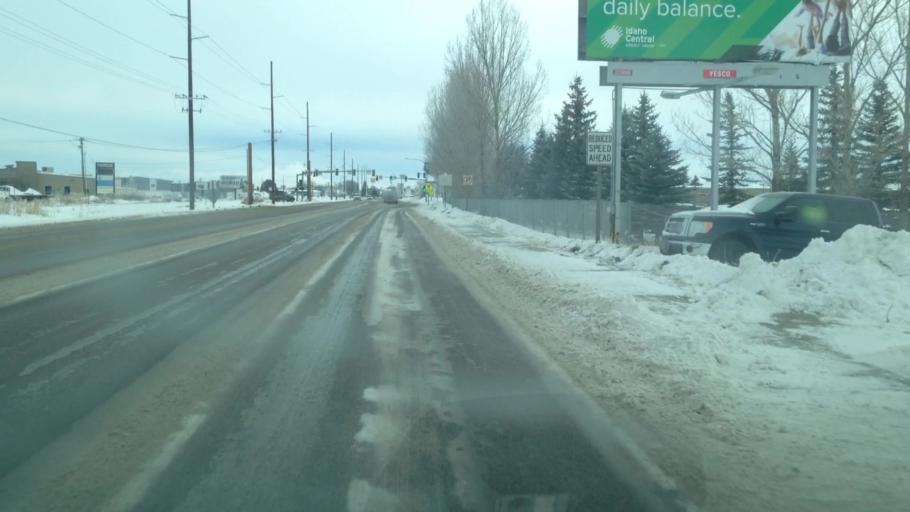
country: US
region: Idaho
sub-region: Madison County
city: Rexburg
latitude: 43.8100
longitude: -111.8038
